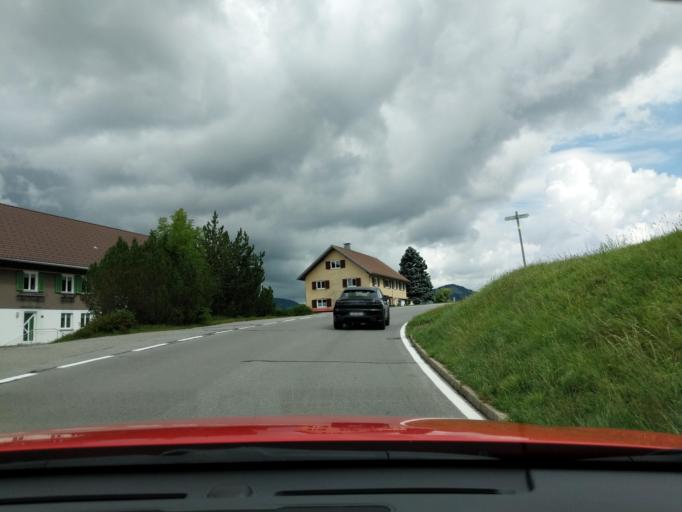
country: AT
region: Vorarlberg
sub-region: Politischer Bezirk Bregenz
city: Riefensberg
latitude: 47.5112
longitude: 9.9527
